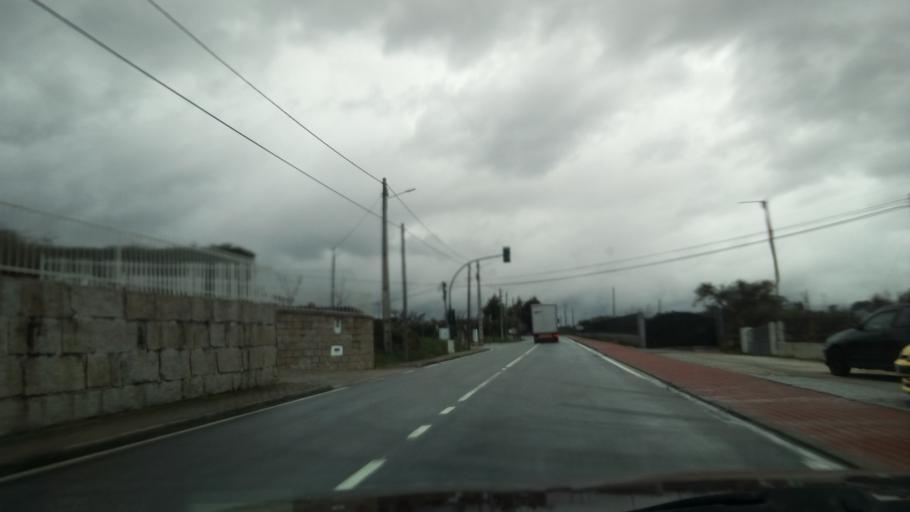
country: PT
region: Guarda
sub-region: Celorico da Beira
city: Celorico da Beira
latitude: 40.6305
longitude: -7.3432
